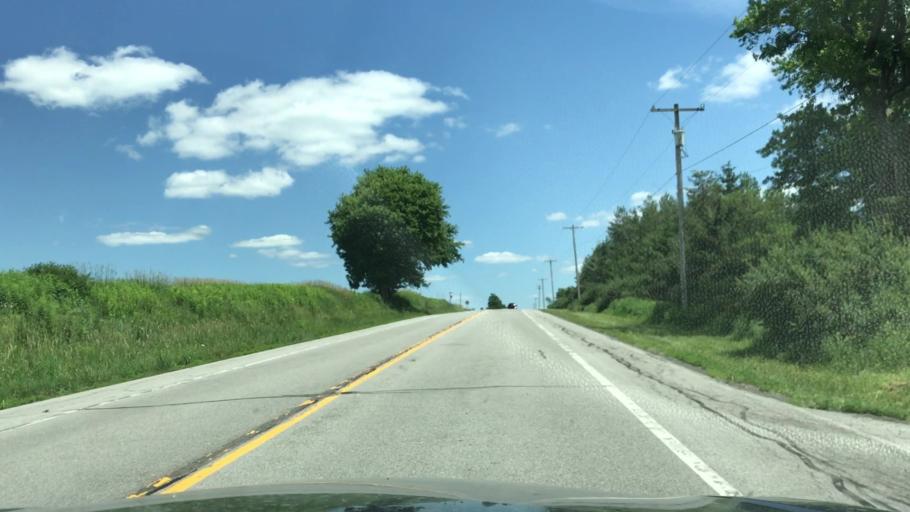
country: US
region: New York
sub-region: Wyoming County
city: Warsaw
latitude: 42.7480
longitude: -78.2337
